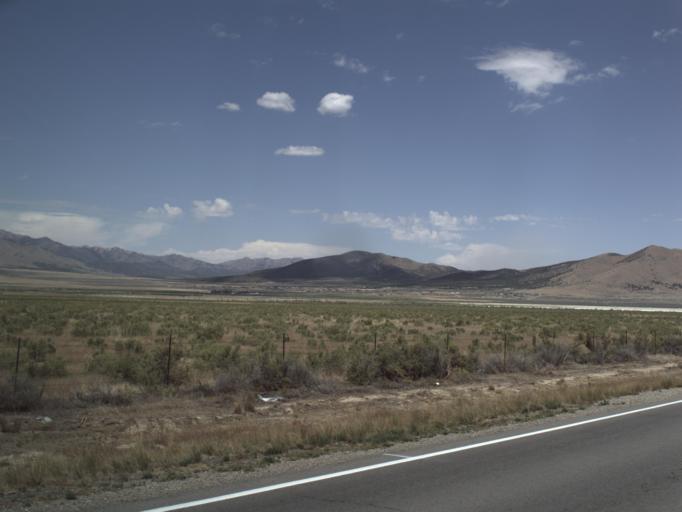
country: US
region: Utah
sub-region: Tooele County
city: Tooele
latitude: 40.3914
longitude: -112.3862
